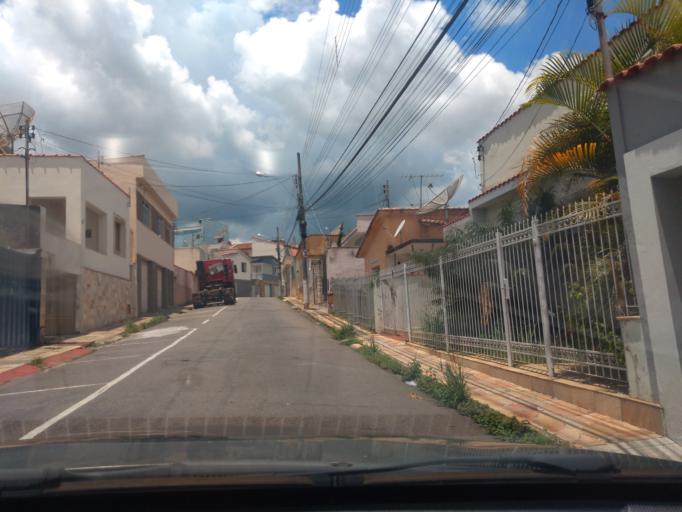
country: BR
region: Minas Gerais
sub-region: Tres Coracoes
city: Tres Coracoes
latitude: -21.6924
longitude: -45.2578
